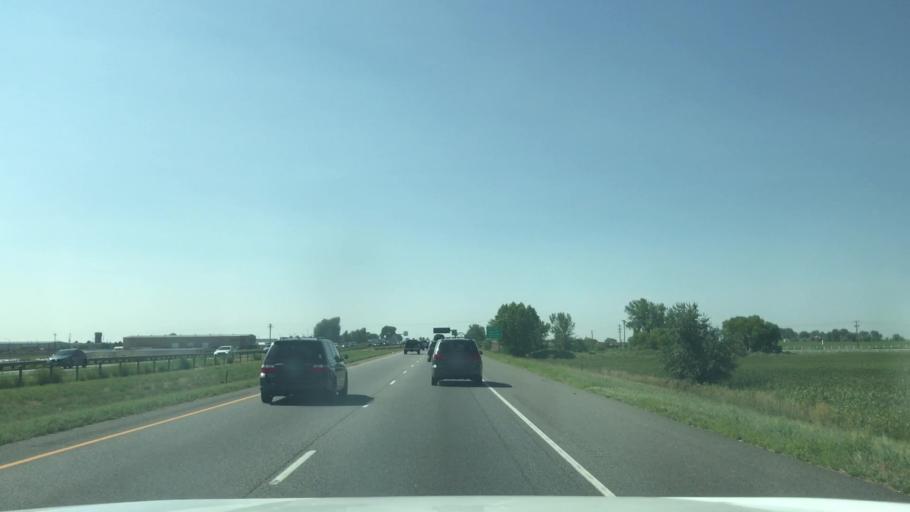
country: US
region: Colorado
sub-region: Weld County
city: Mead
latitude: 40.2218
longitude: -104.9802
